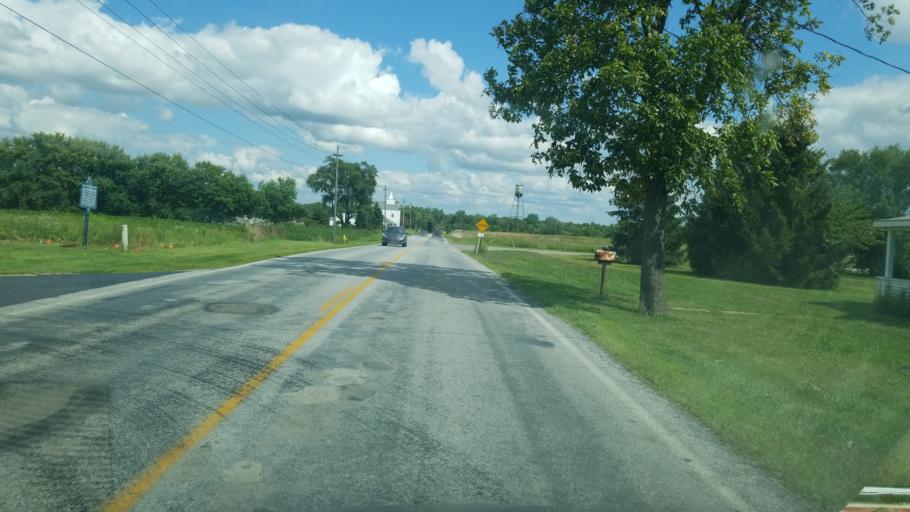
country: US
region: Ohio
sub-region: Allen County
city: Lima
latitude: 40.7883
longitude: -84.1025
